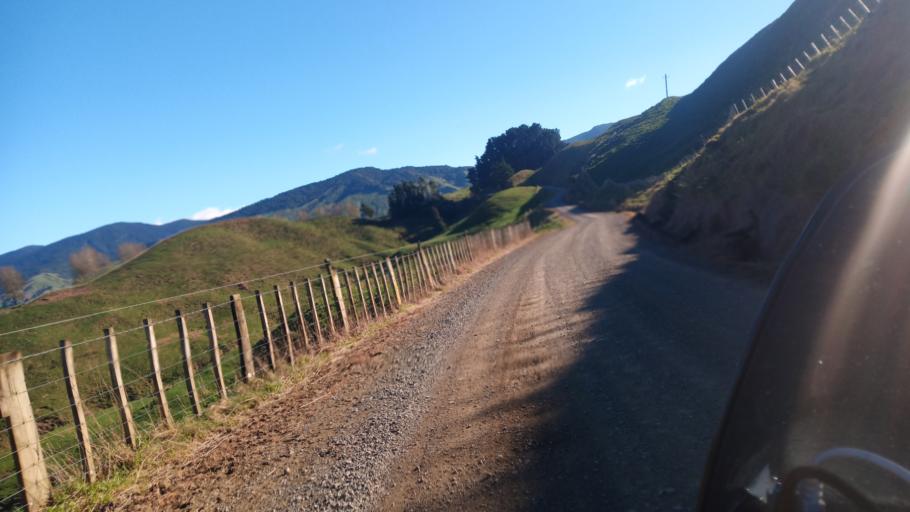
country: NZ
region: Hawke's Bay
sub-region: Wairoa District
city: Wairoa
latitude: -38.7904
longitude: 177.2747
